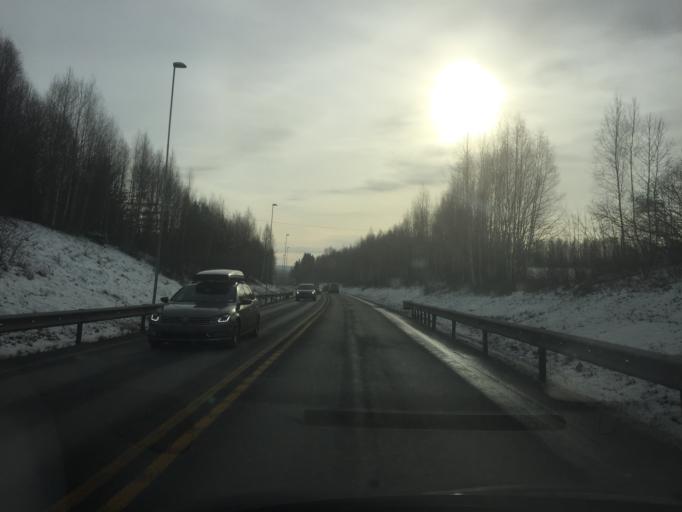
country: NO
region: Hedmark
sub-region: Loten
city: Loten
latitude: 60.7962
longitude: 11.2931
